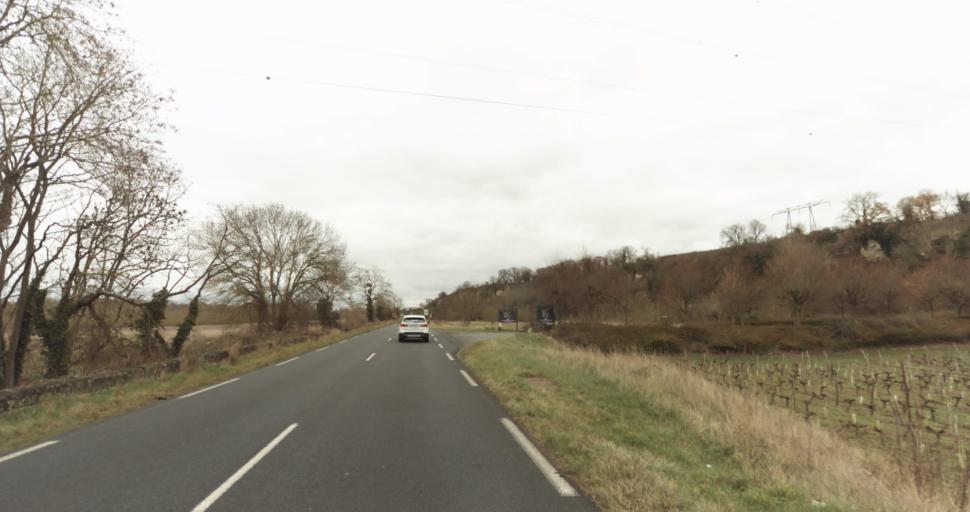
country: FR
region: Pays de la Loire
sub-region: Departement de Maine-et-Loire
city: Varennes-sur-Loire
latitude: 47.2221
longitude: 0.0398
